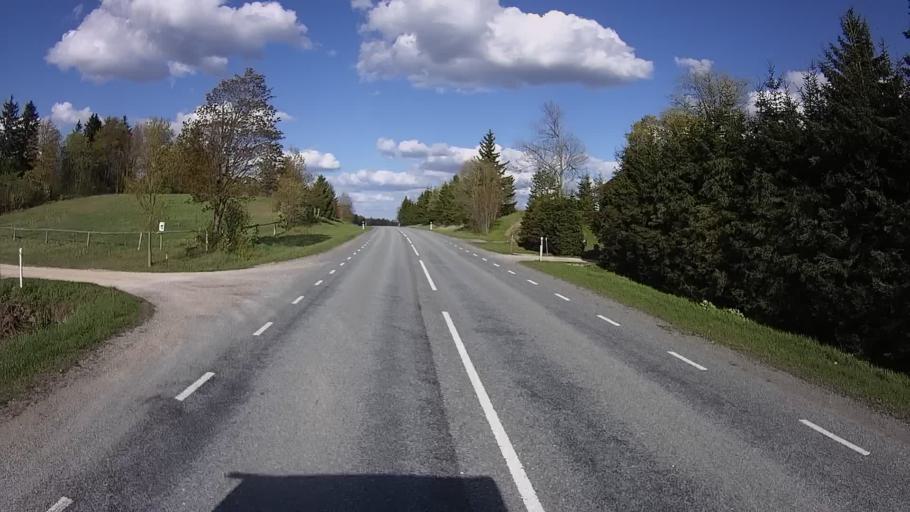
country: EE
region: Jogevamaa
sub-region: Poltsamaa linn
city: Poltsamaa
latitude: 58.6747
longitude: 26.0123
